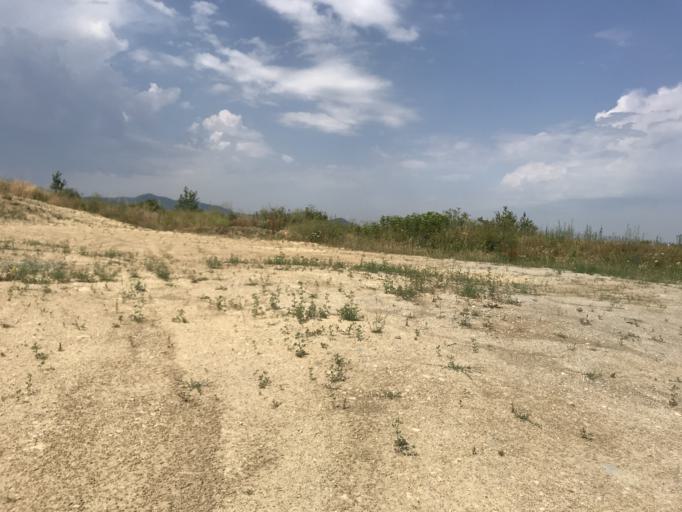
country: ES
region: Basque Country
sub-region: Provincia de Alava
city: Gasteiz / Vitoria
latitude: 42.8311
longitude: -2.6500
